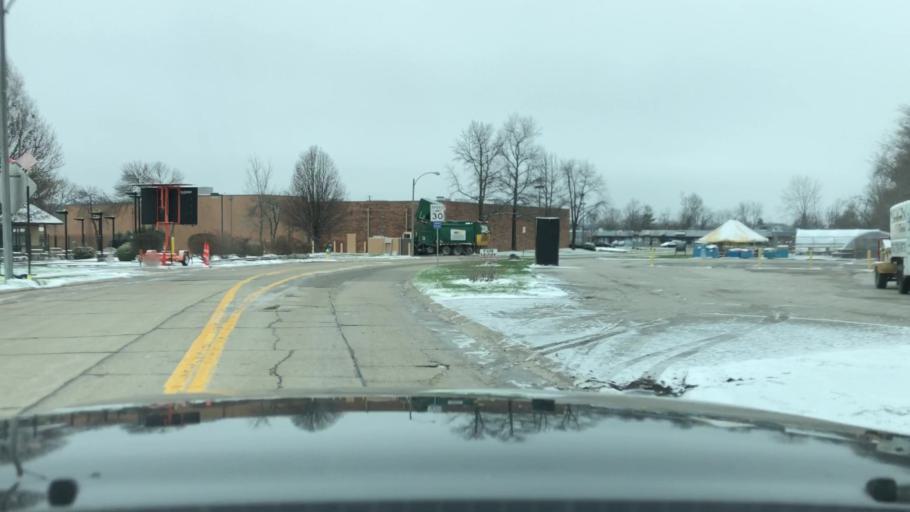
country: US
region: Missouri
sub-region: Saint Charles County
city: Saint Charles
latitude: 38.7890
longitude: -90.5138
